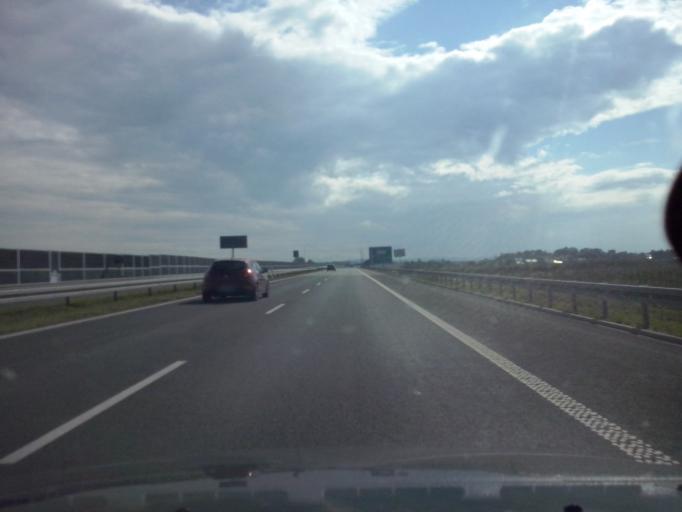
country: PL
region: Lesser Poland Voivodeship
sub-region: Powiat tarnowski
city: Wierzchoslawice
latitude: 50.0230
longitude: 20.8746
